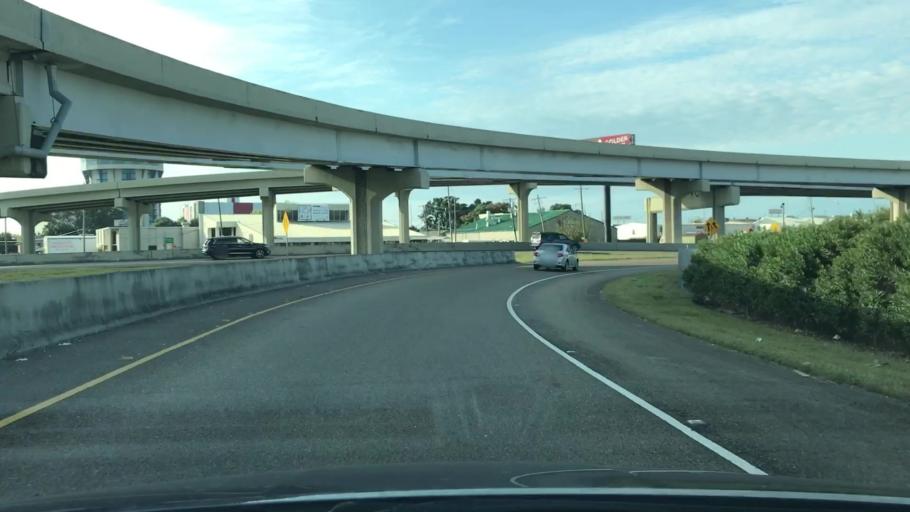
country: US
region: Louisiana
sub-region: Jefferson Parish
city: Metairie
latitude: 29.9996
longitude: -90.1546
